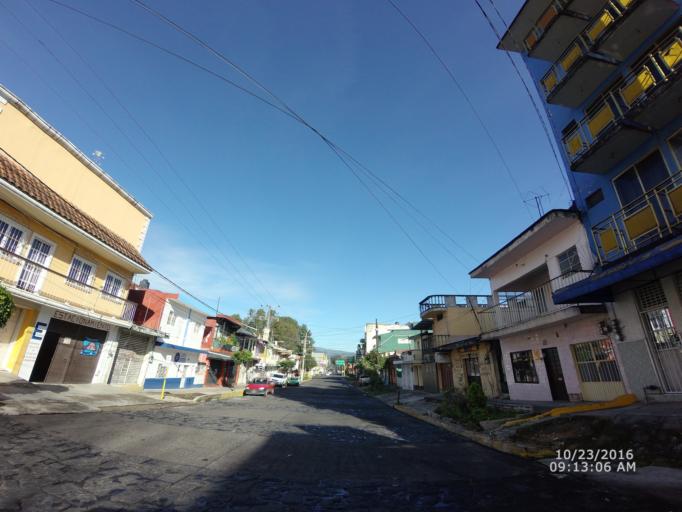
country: TR
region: Canakkale
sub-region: Goekceada
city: Gokceada
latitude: 40.2205
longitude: 26.0270
